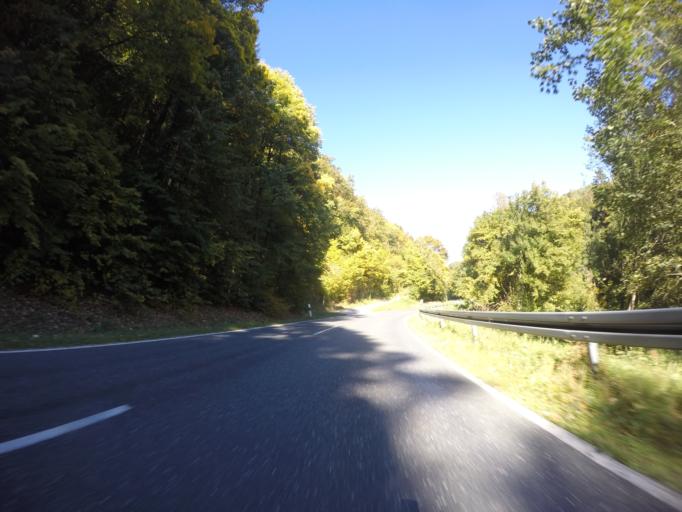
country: DE
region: Bavaria
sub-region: Upper Franconia
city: Gossweinstein
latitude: 49.7846
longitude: 11.3320
